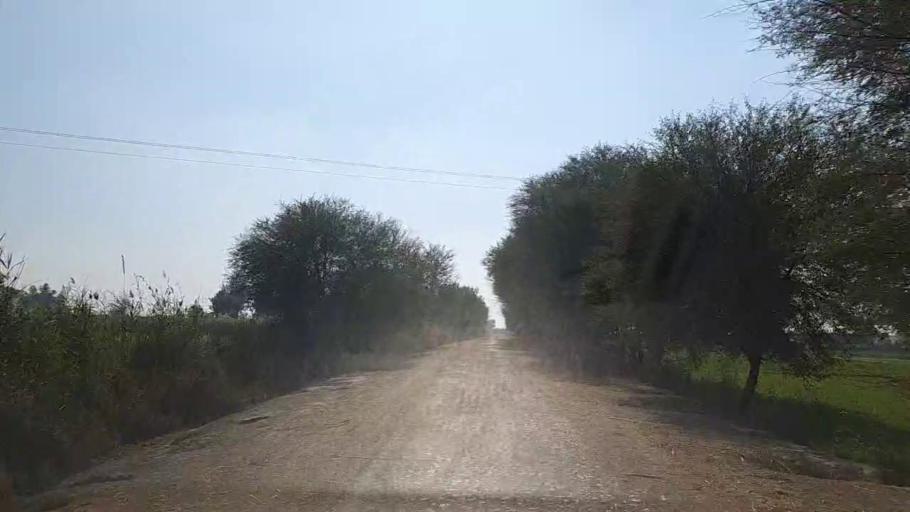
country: PK
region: Sindh
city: Daur
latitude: 26.5049
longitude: 68.3402
